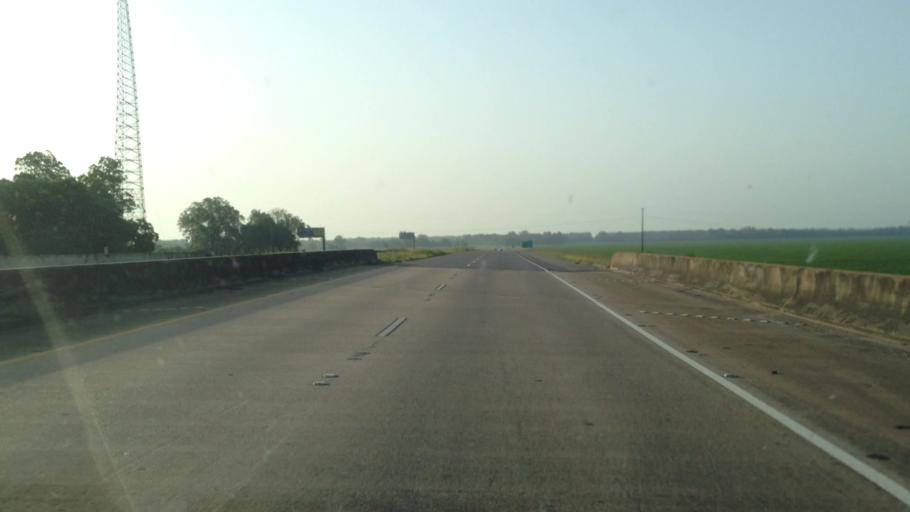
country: US
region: Louisiana
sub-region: Rapides Parish
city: Boyce
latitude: 31.3924
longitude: -92.6930
